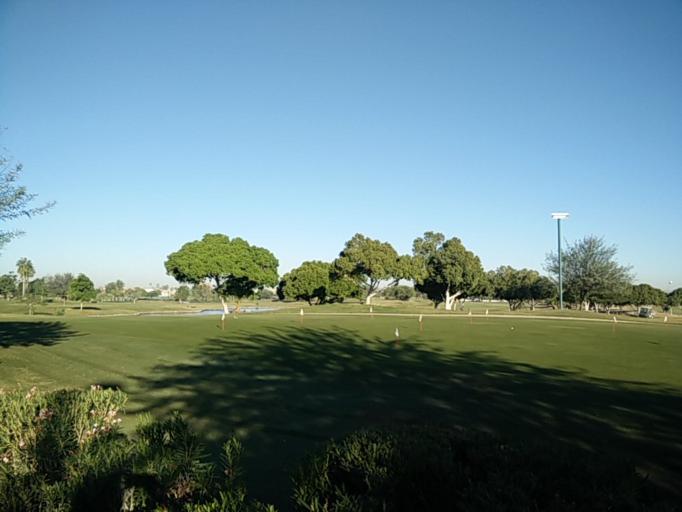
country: MX
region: Sonora
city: Hermosillo
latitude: 29.0719
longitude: -111.0020
